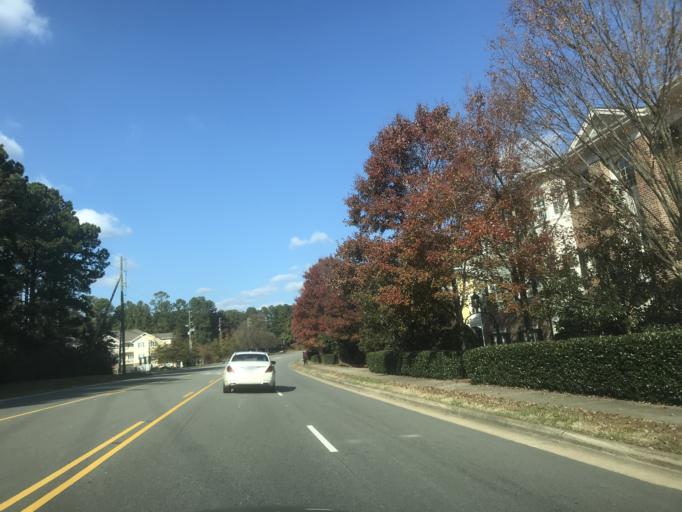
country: US
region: North Carolina
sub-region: Wake County
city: West Raleigh
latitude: 35.8812
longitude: -78.6615
